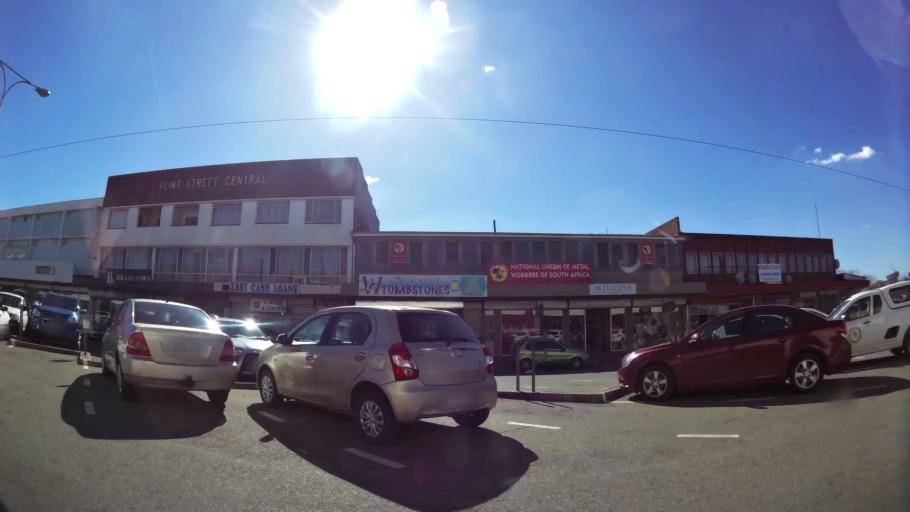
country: ZA
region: Gauteng
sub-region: West Rand District Municipality
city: Carletonville
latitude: -26.3568
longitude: 27.3992
